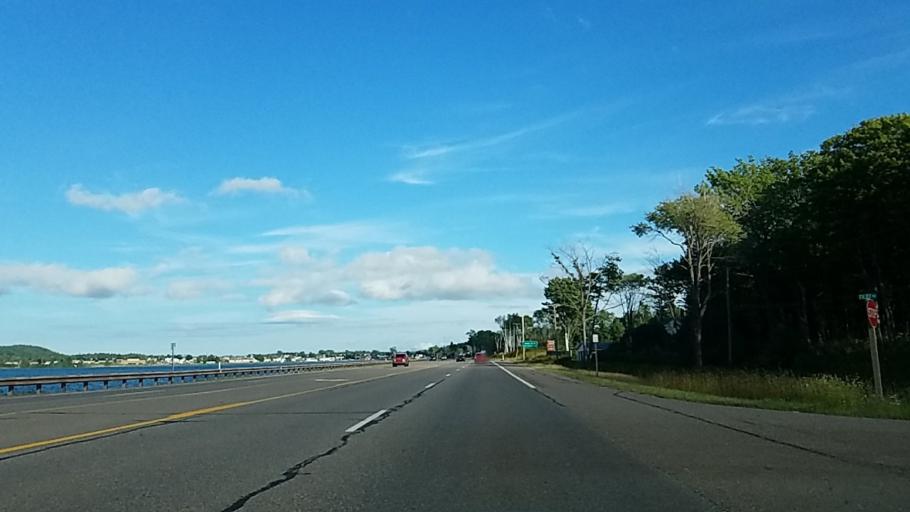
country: US
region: Michigan
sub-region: Marquette County
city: Negaunee
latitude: 46.5099
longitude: -87.6313
